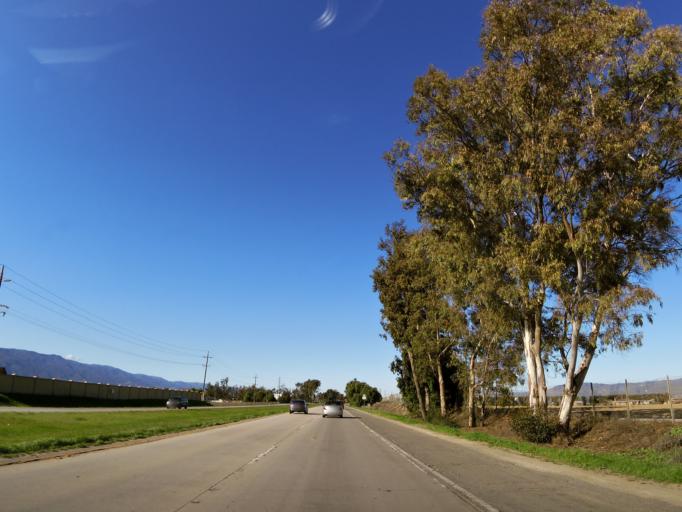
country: US
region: California
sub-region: Monterey County
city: Greenfield
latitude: 36.3325
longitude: -121.2474
